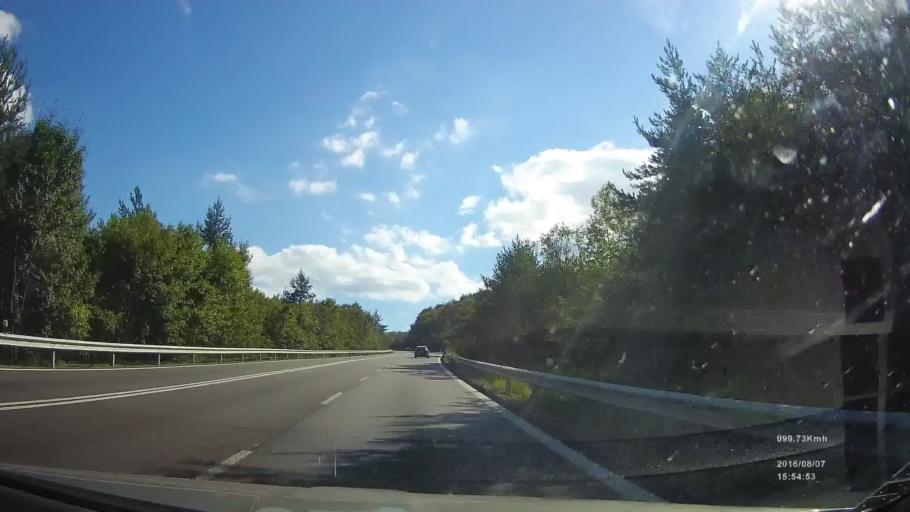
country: SK
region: Presovsky
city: Giraltovce
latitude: 49.0815
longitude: 21.4431
